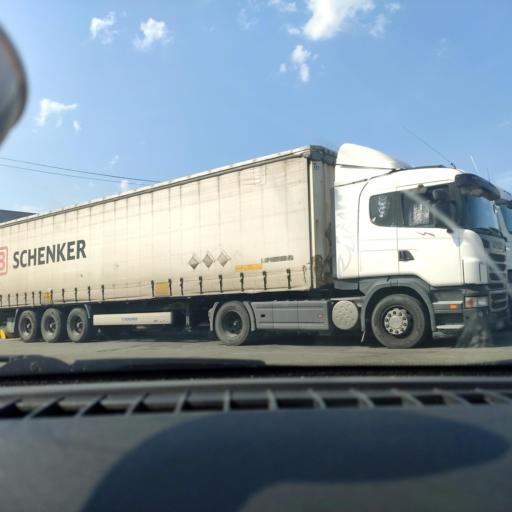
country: RU
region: Samara
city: Samara
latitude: 53.0926
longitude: 50.1265
